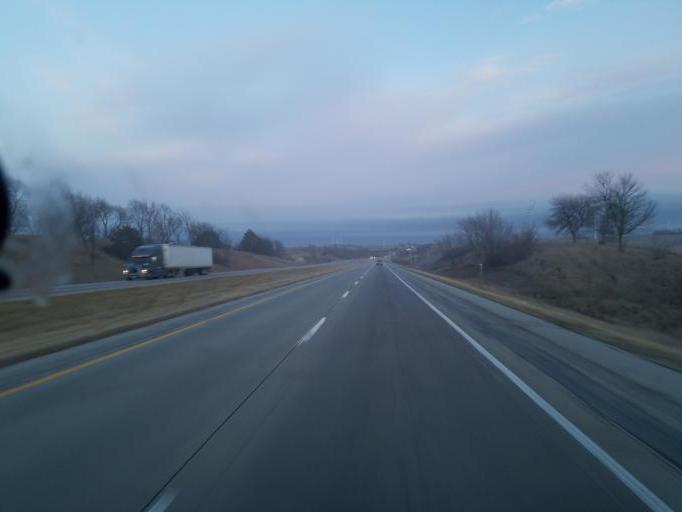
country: US
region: Iowa
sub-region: Pottawattamie County
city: Avoca
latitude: 41.4985
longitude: -95.2931
